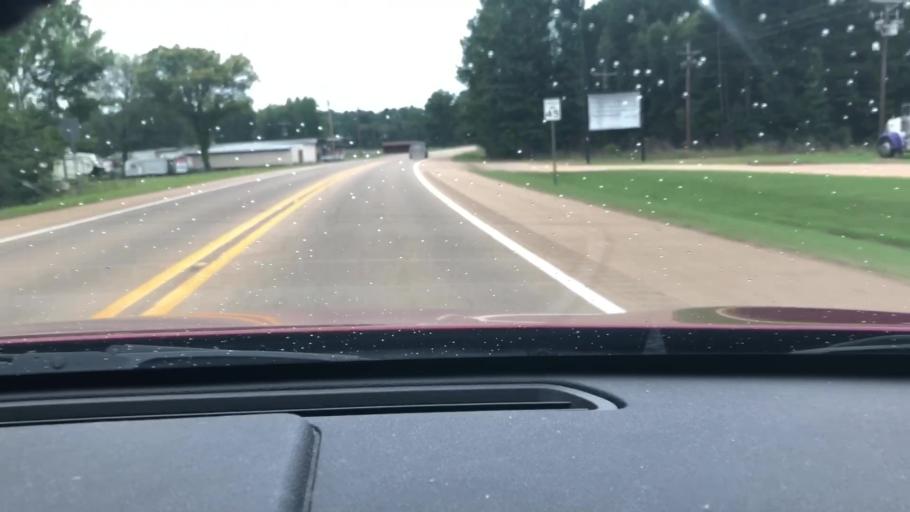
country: US
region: Arkansas
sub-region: Lafayette County
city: Stamps
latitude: 33.3675
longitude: -93.5154
